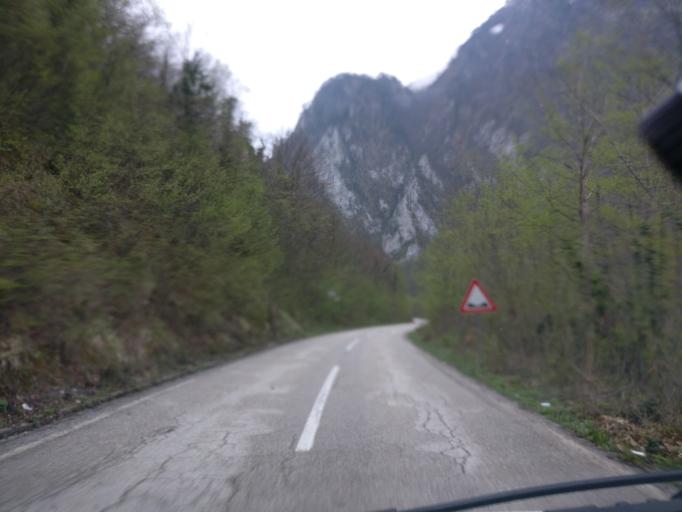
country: ME
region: Opstina Pluzine
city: Pluzine
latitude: 43.3068
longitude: 18.8513
